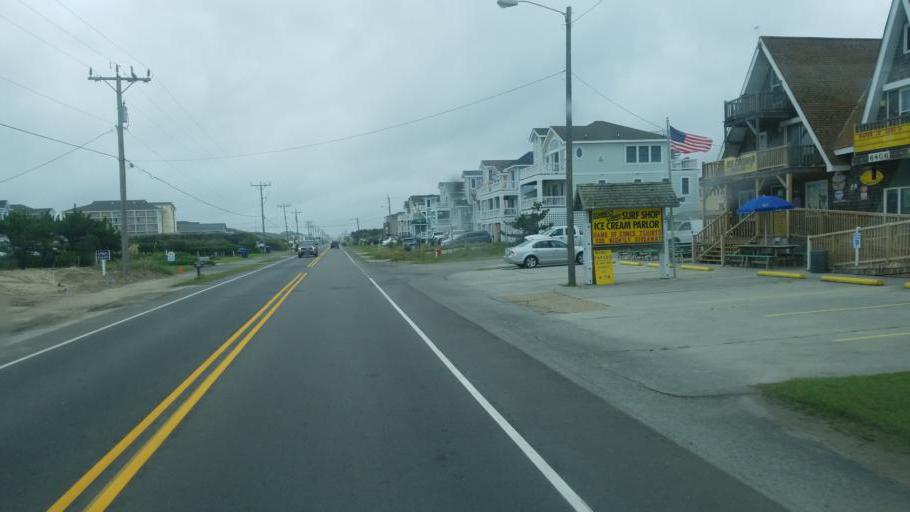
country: US
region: North Carolina
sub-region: Dare County
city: Nags Head
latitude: 35.9219
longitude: -75.6043
